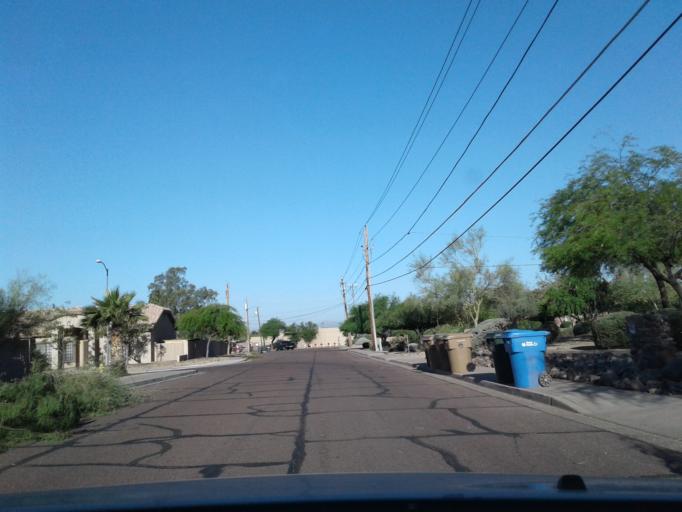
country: US
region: Arizona
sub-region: Maricopa County
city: Paradise Valley
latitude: 33.5420
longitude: -112.0384
